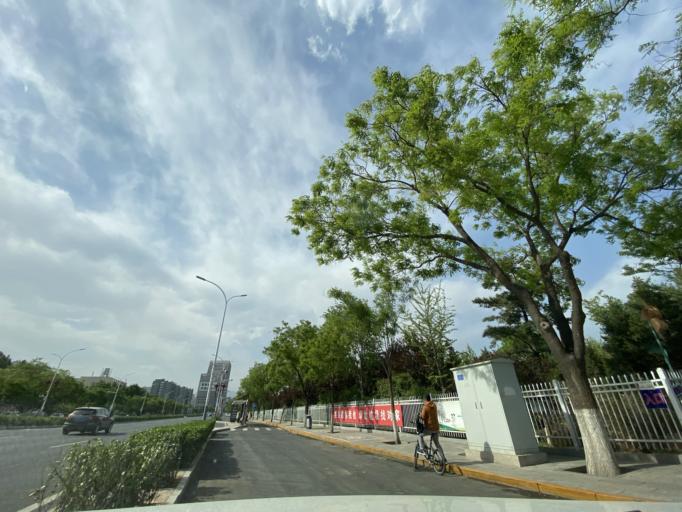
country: CN
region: Beijing
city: Dayu
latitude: 39.9368
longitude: 116.1045
